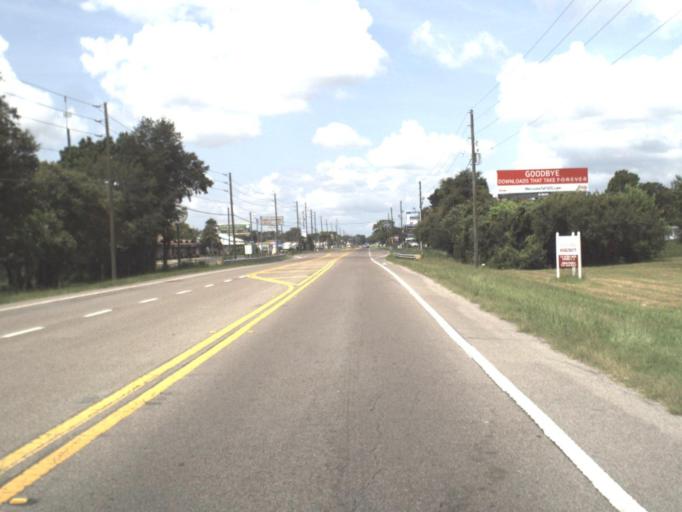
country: US
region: Florida
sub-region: Pasco County
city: Zephyrhills West
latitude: 28.2271
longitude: -82.2299
